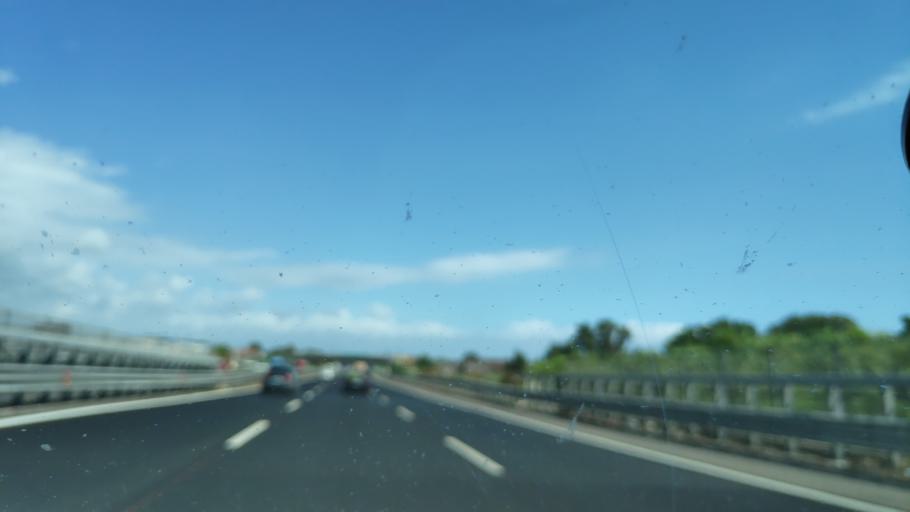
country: IT
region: Campania
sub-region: Provincia di Salerno
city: Pontecagnano
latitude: 40.6533
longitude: 14.8716
